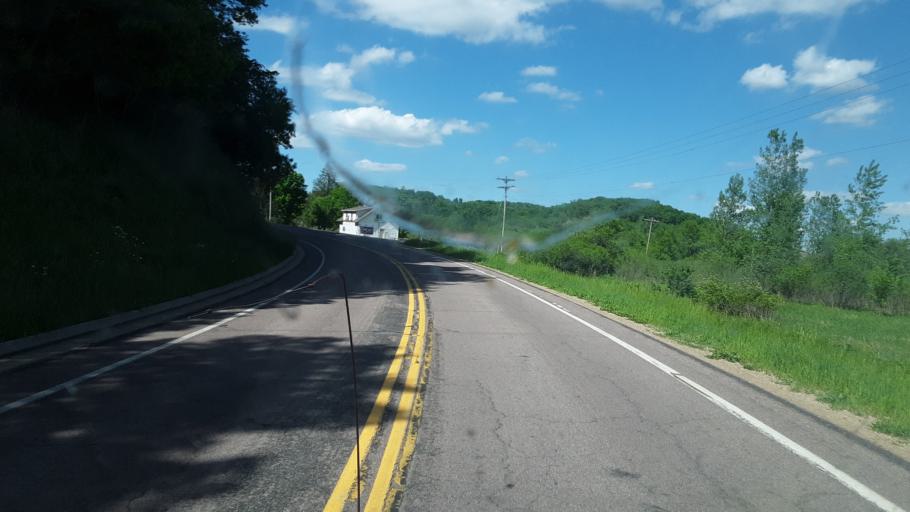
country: US
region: Wisconsin
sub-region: Richland County
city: Richland Center
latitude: 43.4093
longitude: -90.2403
